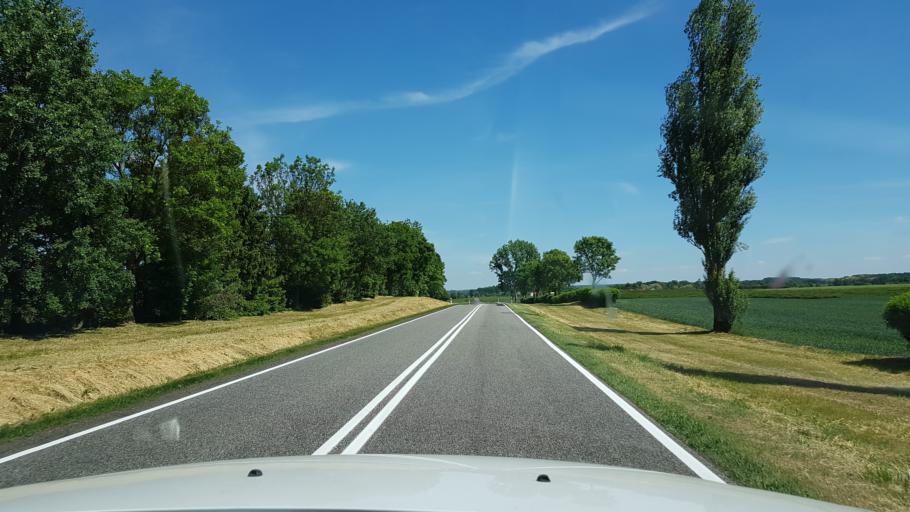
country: PL
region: West Pomeranian Voivodeship
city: Trzcinsko Zdroj
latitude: 52.9584
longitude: 14.5304
